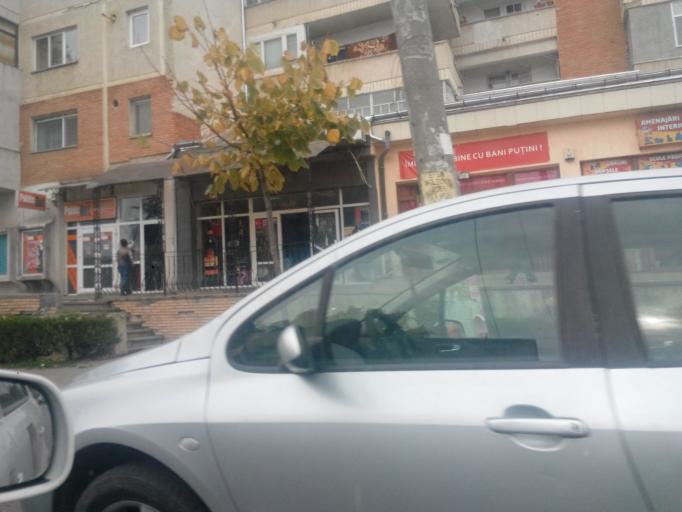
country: RO
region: Vaslui
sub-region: Municipiul Husi
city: Husi
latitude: 46.6713
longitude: 28.0635
